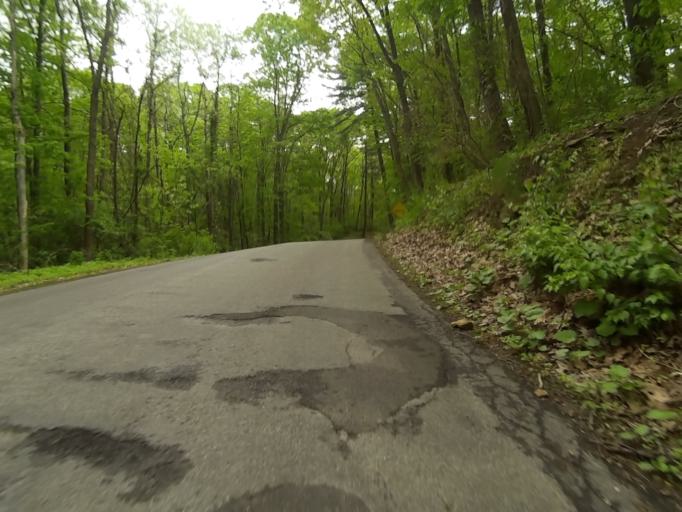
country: US
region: Pennsylvania
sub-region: Centre County
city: Zion
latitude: 40.9758
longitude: -77.6232
